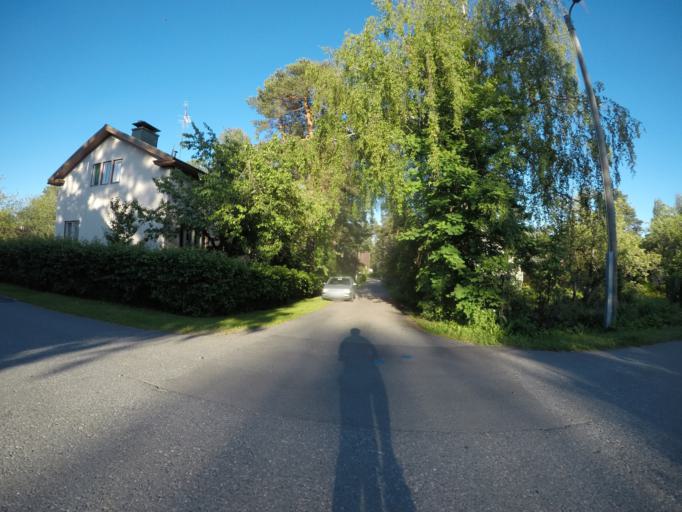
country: FI
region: Haeme
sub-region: Haemeenlinna
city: Haemeenlinna
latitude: 60.9837
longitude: 24.4519
